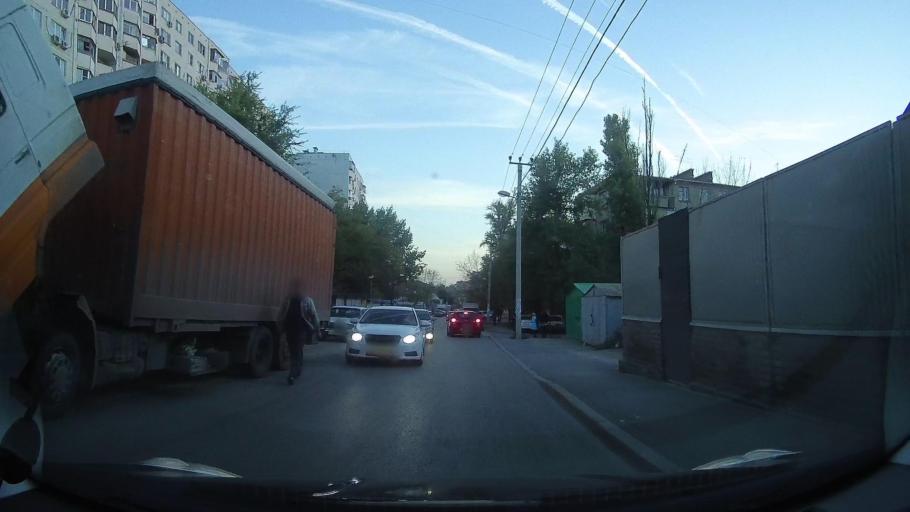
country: RU
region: Rostov
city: Rostov-na-Donu
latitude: 47.2518
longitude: 39.6886
